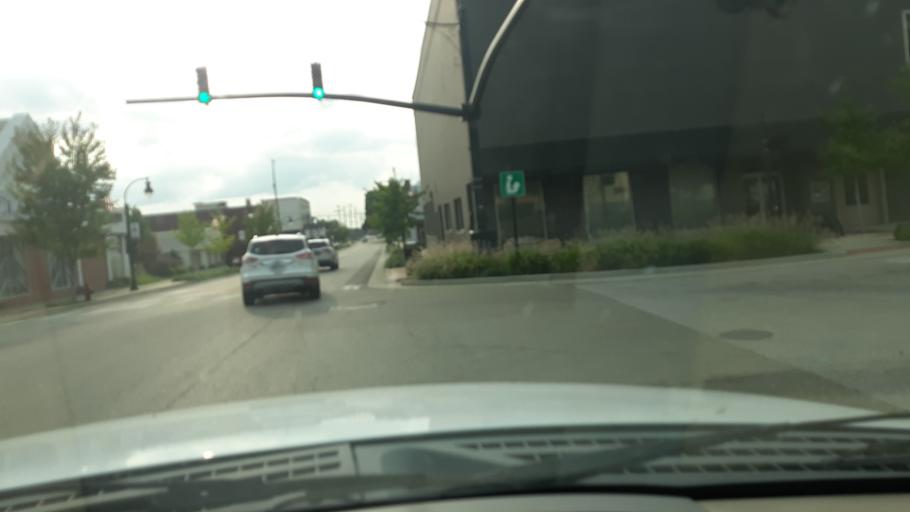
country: US
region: Indiana
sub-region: Gibson County
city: Princeton
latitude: 38.3553
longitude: -87.5685
